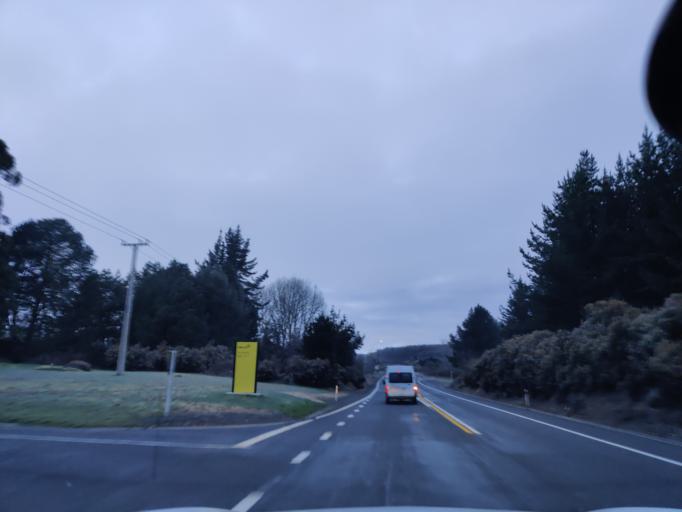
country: NZ
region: Waikato
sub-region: South Waikato District
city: Tokoroa
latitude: -38.3947
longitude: 176.0200
